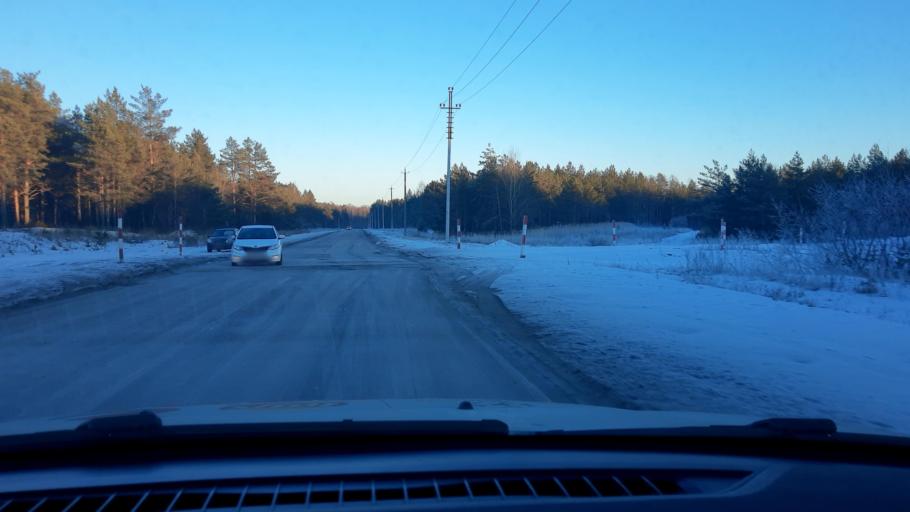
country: RU
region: Nizjnij Novgorod
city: Novosmolinskiy
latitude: 56.3193
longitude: 43.0050
